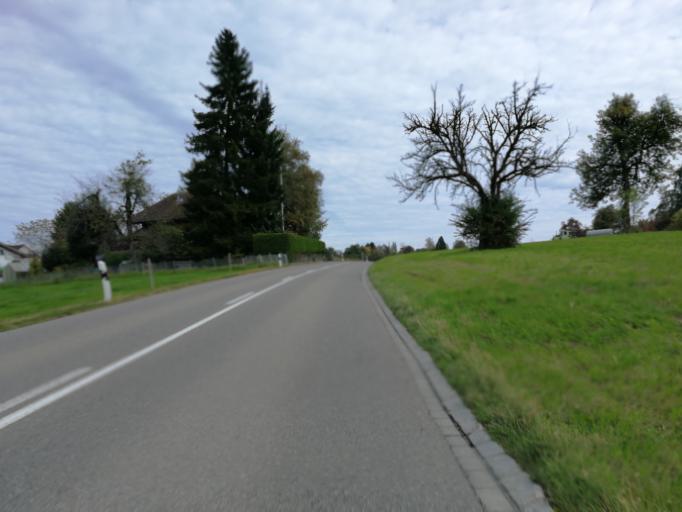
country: CH
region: Zurich
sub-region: Bezirk Meilen
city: Oetwil am See
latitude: 47.2656
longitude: 8.7389
